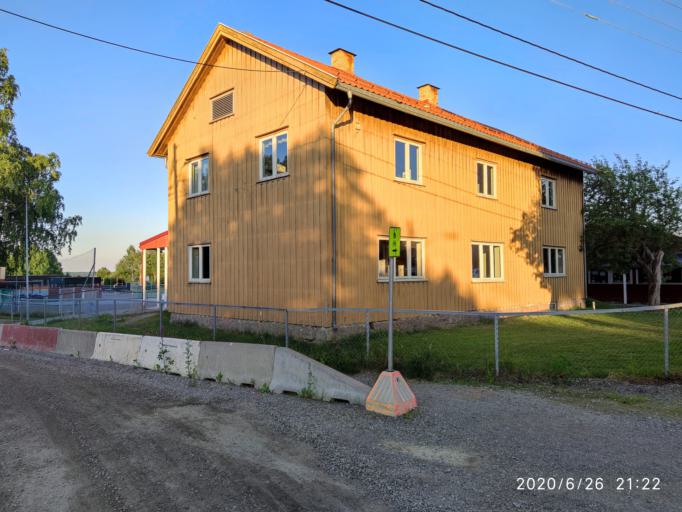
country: NO
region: Akershus
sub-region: Nannestad
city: Teigebyen
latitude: 60.1713
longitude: 10.9928
